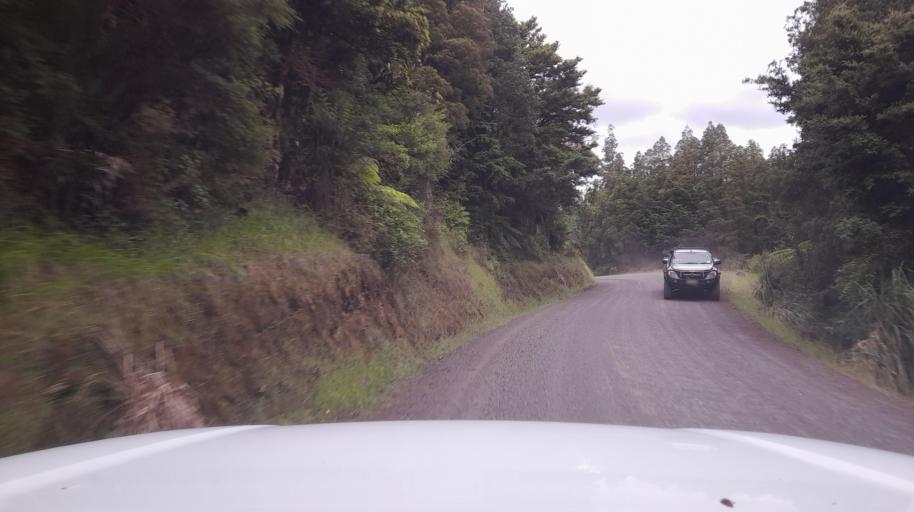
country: NZ
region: Northland
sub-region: Far North District
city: Kaitaia
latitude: -35.3202
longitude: 173.3497
